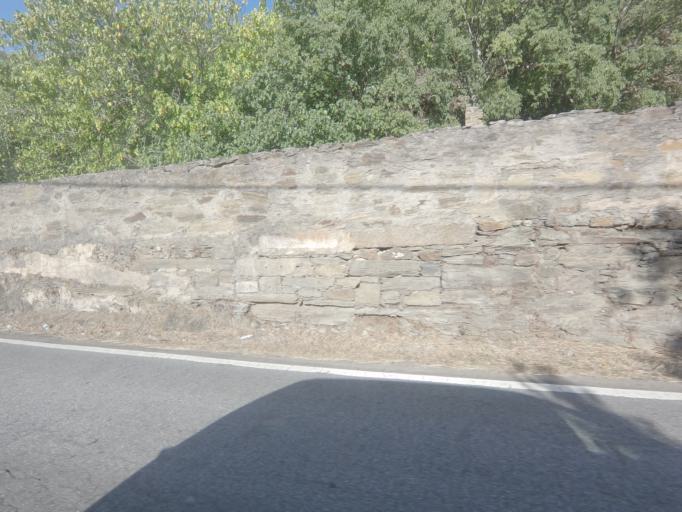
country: PT
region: Viseu
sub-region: Tabuaco
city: Tabuaco
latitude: 41.1804
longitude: -7.5503
